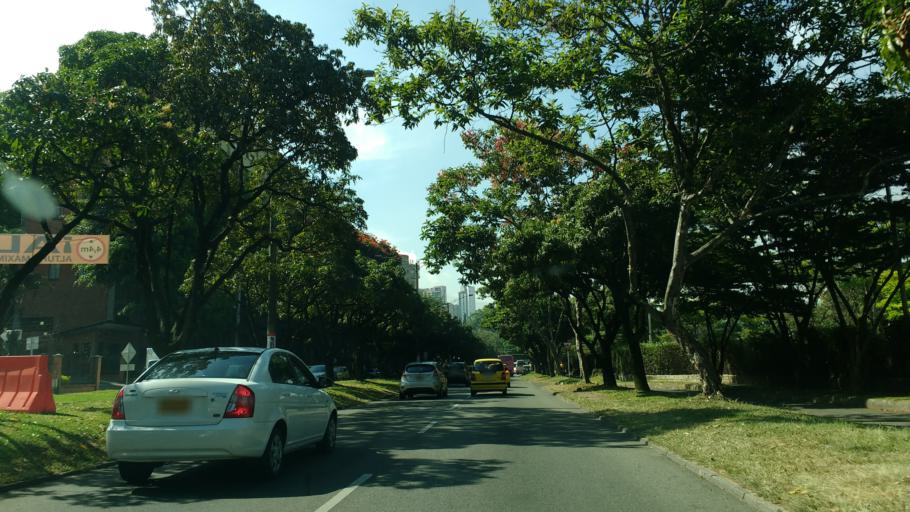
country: CO
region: Antioquia
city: Itagui
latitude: 6.2018
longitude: -75.5774
